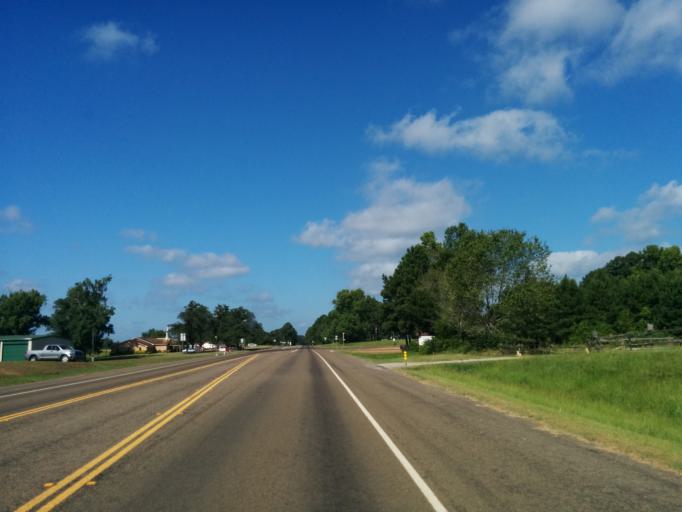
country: US
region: Texas
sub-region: Sabine County
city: Milam
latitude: 31.4206
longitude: -93.9737
